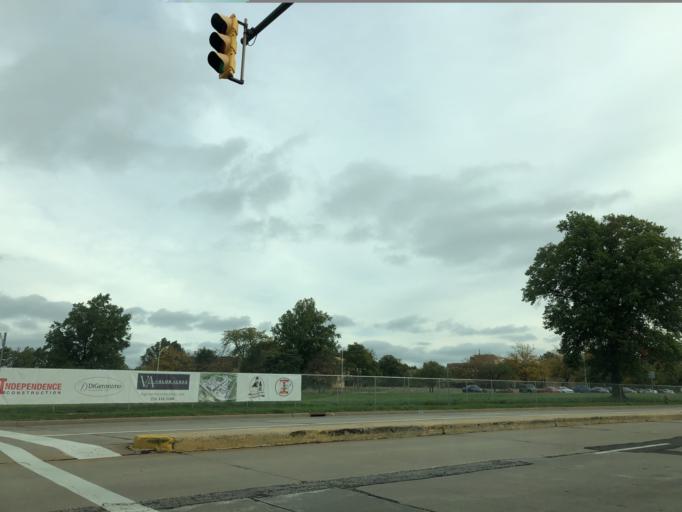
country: US
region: Ohio
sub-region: Cuyahoga County
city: Brecksville
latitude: 41.2893
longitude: -81.6331
